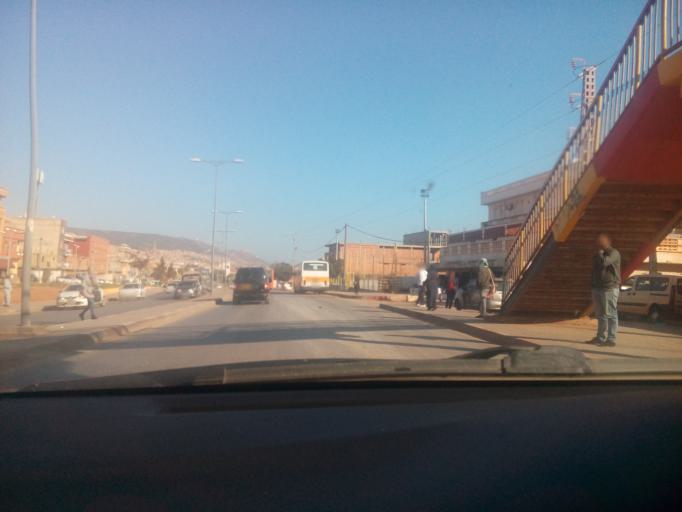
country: DZ
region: Oran
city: Oran
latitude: 35.6638
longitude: -0.6841
